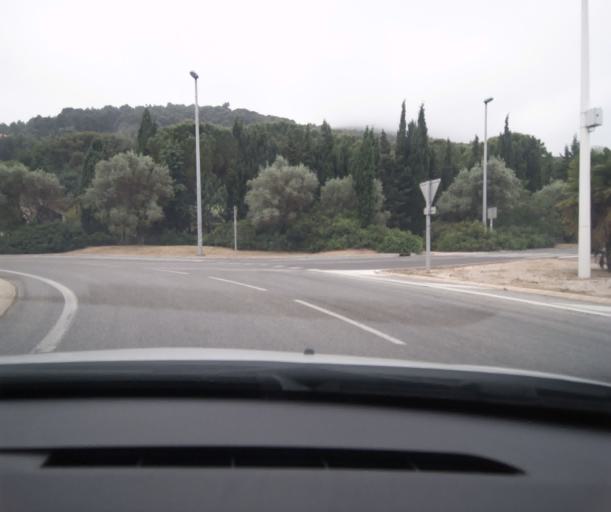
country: FR
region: Provence-Alpes-Cote d'Azur
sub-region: Departement du Var
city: La Valette-du-Var
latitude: 43.1476
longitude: 5.9780
